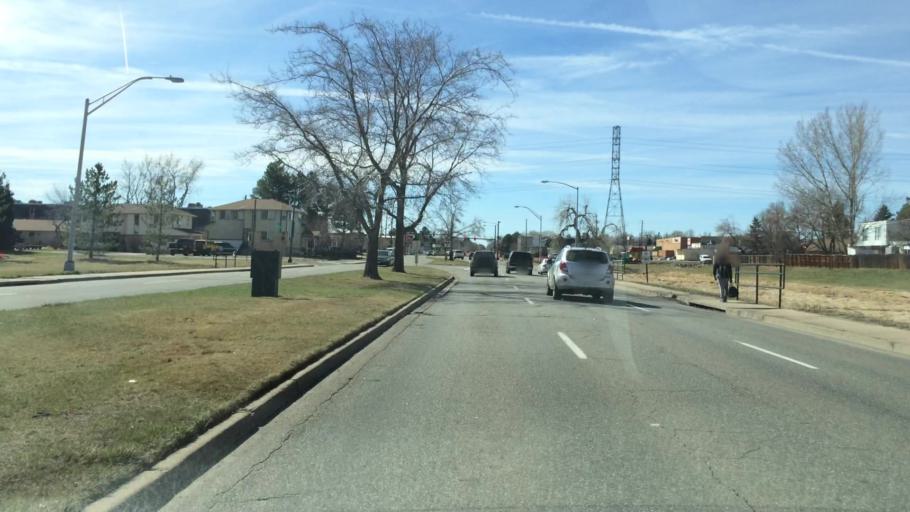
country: US
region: Colorado
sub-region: Arapahoe County
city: Glendale
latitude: 39.6809
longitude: -104.9130
